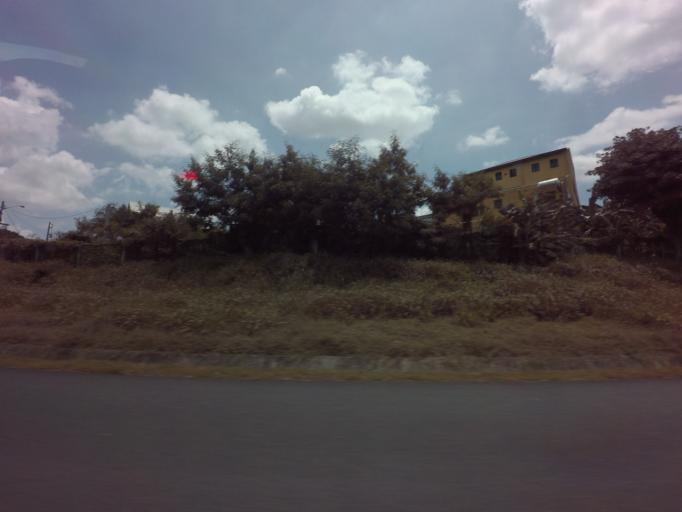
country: PH
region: Calabarzon
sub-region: Province of Laguna
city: San Pedro
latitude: 14.4072
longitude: 121.0410
